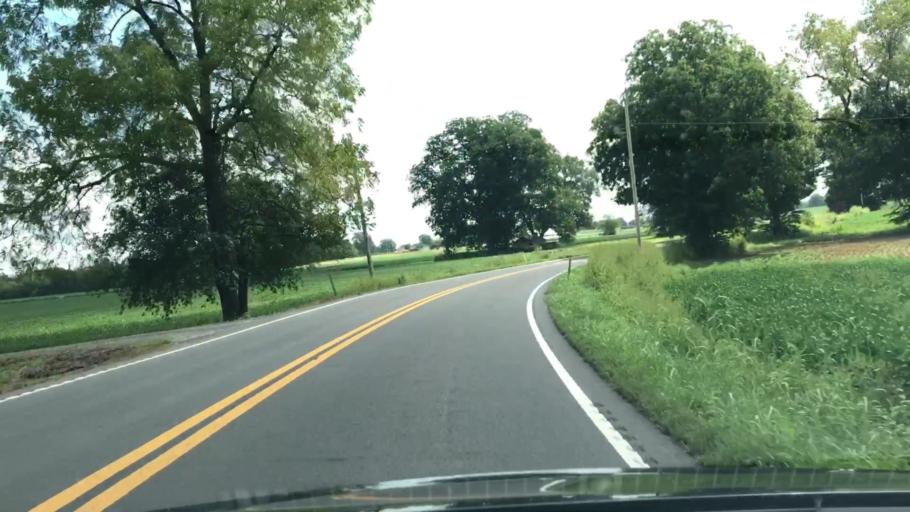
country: US
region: Tennessee
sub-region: Robertson County
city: Springfield
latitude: 36.5627
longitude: -86.8407
